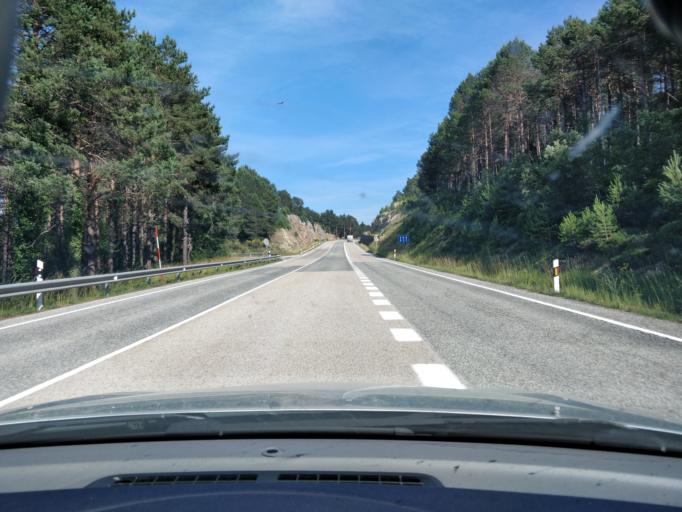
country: ES
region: Cantabria
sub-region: Provincia de Cantabria
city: San Martin de Elines
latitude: 42.9573
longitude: -3.7678
